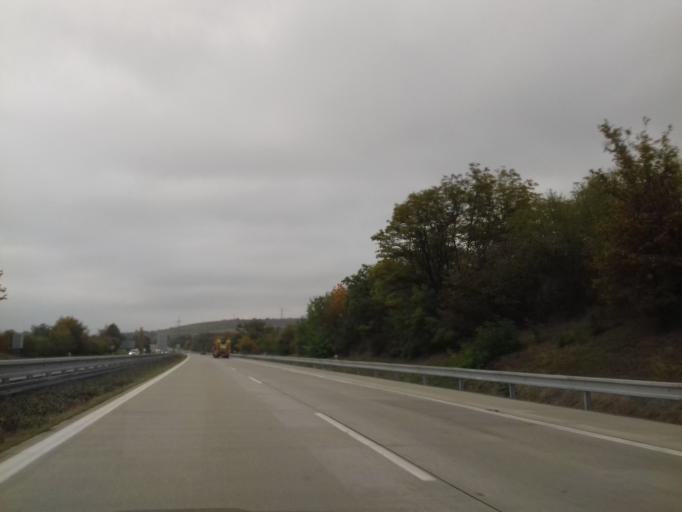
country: CZ
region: South Moravian
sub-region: Okres Breclav
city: Hustopece
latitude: 48.9239
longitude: 16.7631
